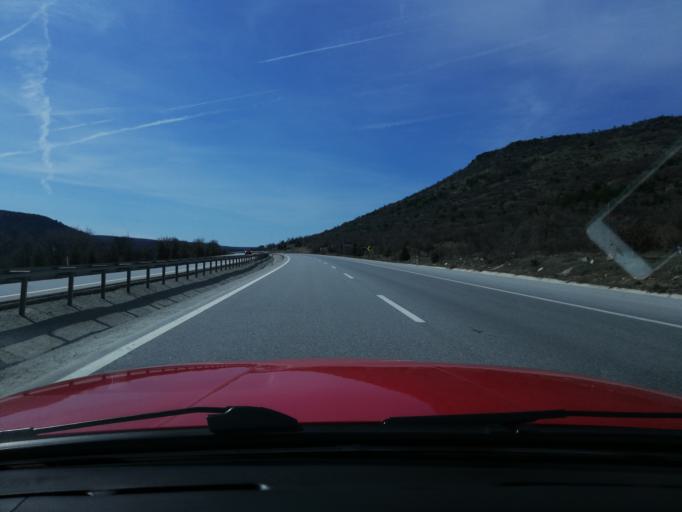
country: TR
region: Kuetahya
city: Sabuncu
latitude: 39.6034
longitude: 30.1466
